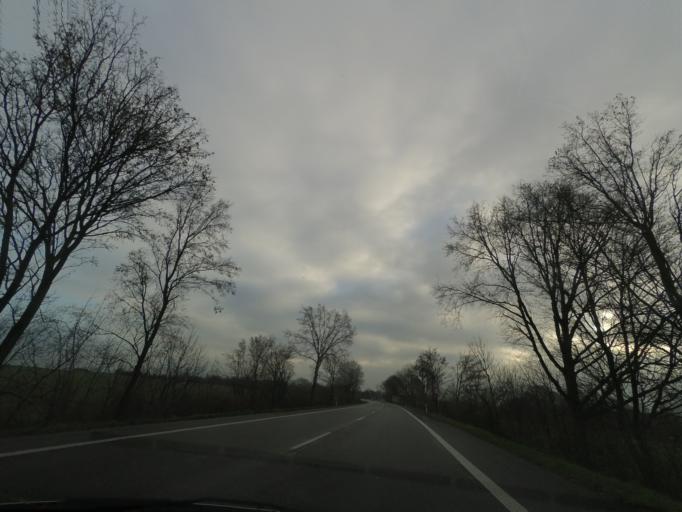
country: DE
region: North Rhine-Westphalia
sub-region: Regierungsbezirk Dusseldorf
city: Neubrueck
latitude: 51.1435
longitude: 6.6052
